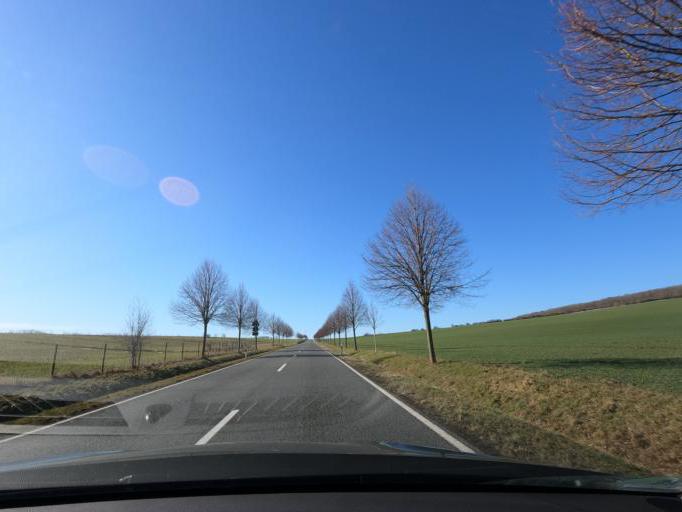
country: DE
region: Saxony-Anhalt
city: Osterwieck
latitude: 51.9826
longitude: 10.7664
